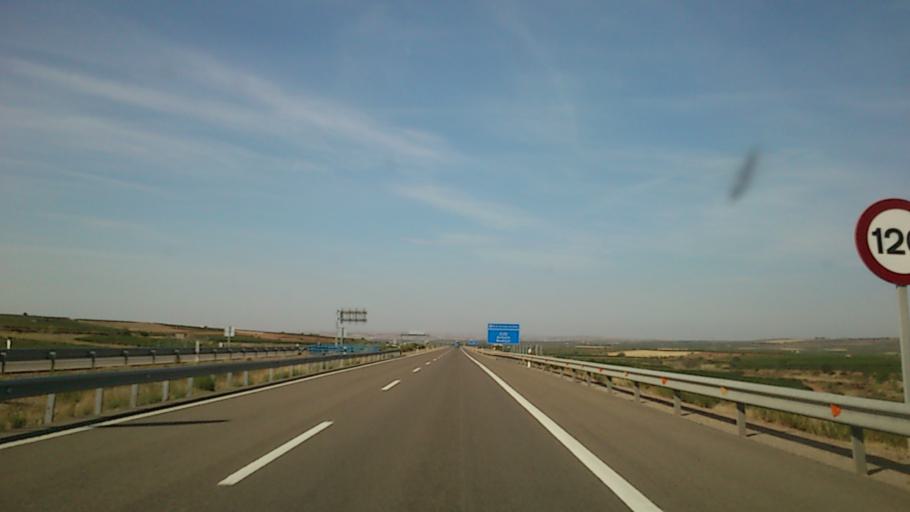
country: ES
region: Aragon
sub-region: Provincia de Zaragoza
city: Paniza
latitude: 41.3063
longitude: -1.2116
